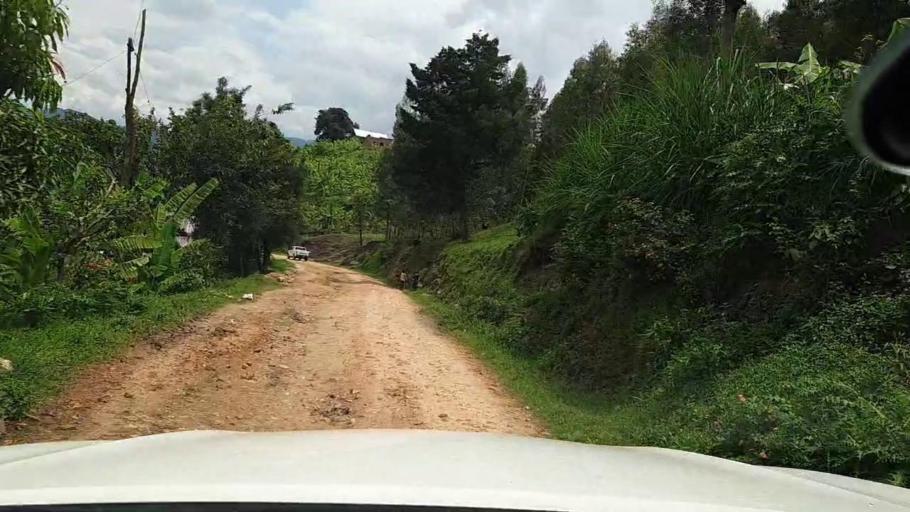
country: RW
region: Western Province
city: Kibuye
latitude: -2.0841
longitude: 29.4170
